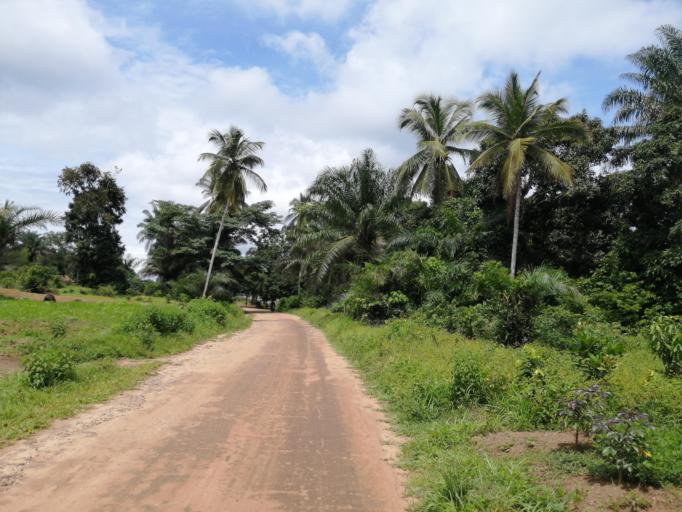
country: SL
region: Northern Province
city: Pepel
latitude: 8.6119
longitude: -13.0495
